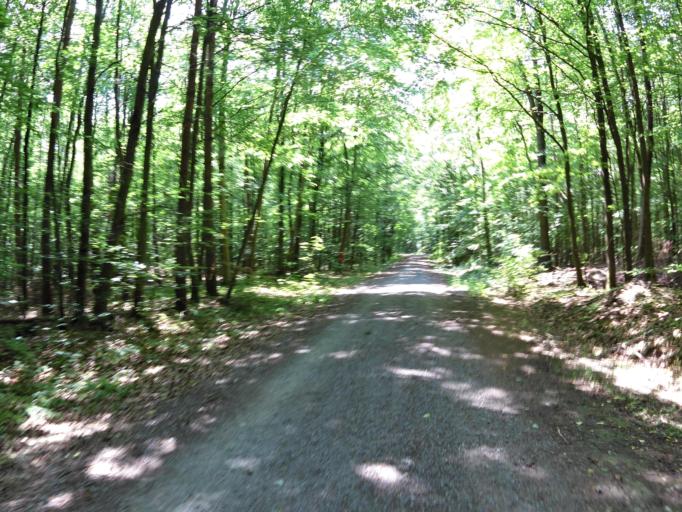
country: DE
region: Bavaria
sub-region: Regierungsbezirk Unterfranken
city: Kleinrinderfeld
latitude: 49.7178
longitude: 9.8553
